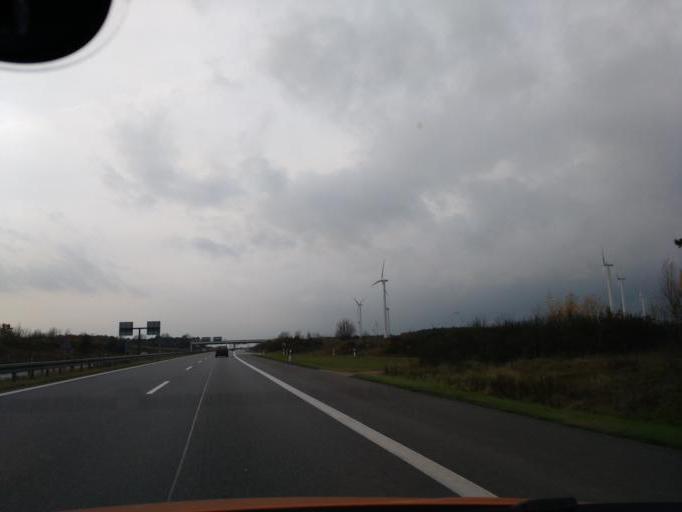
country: DE
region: Brandenburg
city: Wittstock
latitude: 53.1353
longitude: 12.4546
